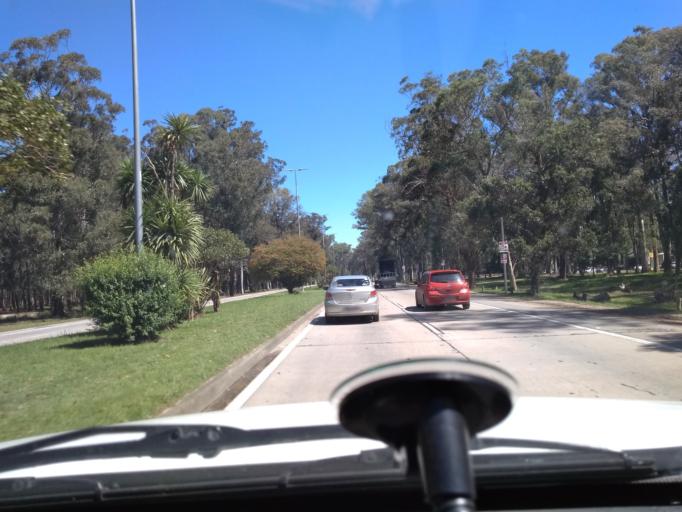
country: UY
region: Canelones
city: Barra de Carrasco
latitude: -34.8539
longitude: -56.0273
